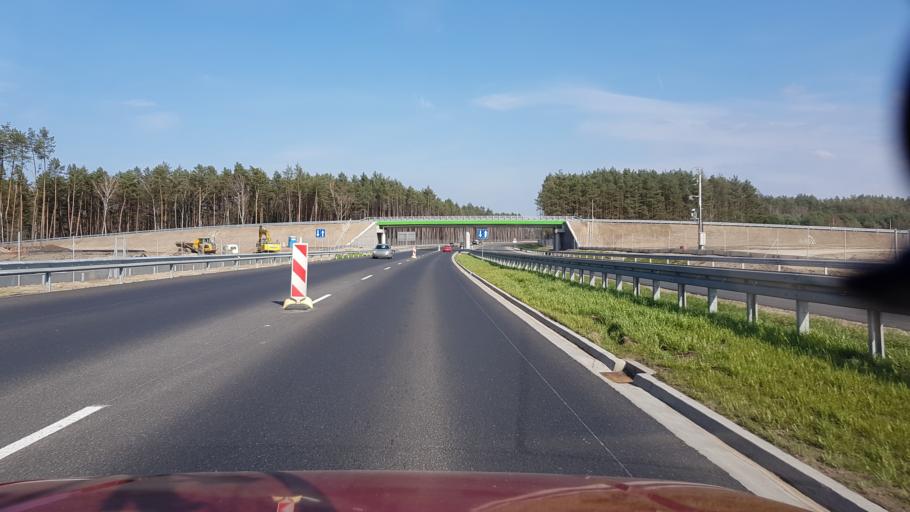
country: PL
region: West Pomeranian Voivodeship
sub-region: Powiat goleniowski
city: Mosty
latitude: 53.6115
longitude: 14.9044
